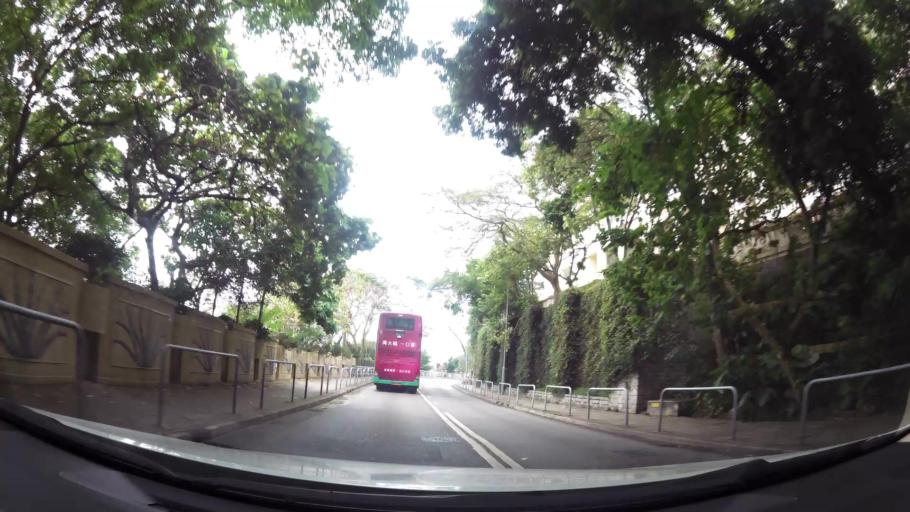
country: HK
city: Hong Kong
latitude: 22.2730
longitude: 114.1198
